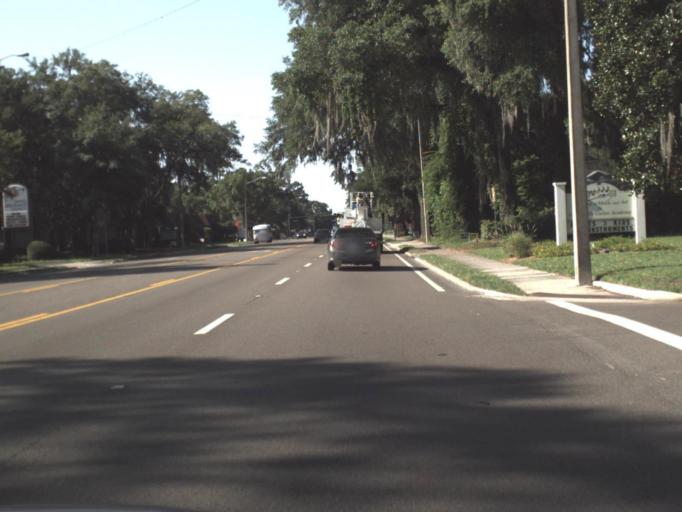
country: US
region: Florida
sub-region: Alachua County
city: Gainesville
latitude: 29.6639
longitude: -82.3392
